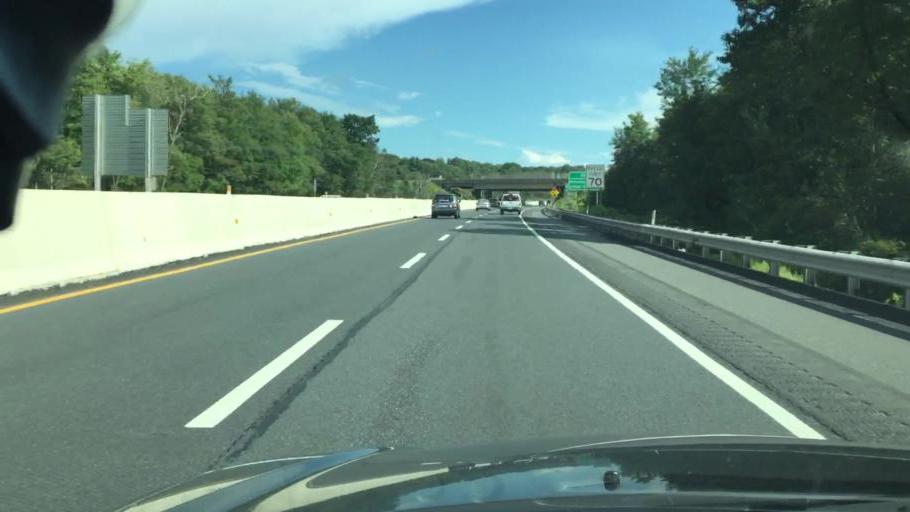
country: US
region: Pennsylvania
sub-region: Luzerne County
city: White Haven
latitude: 41.0699
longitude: -75.6966
